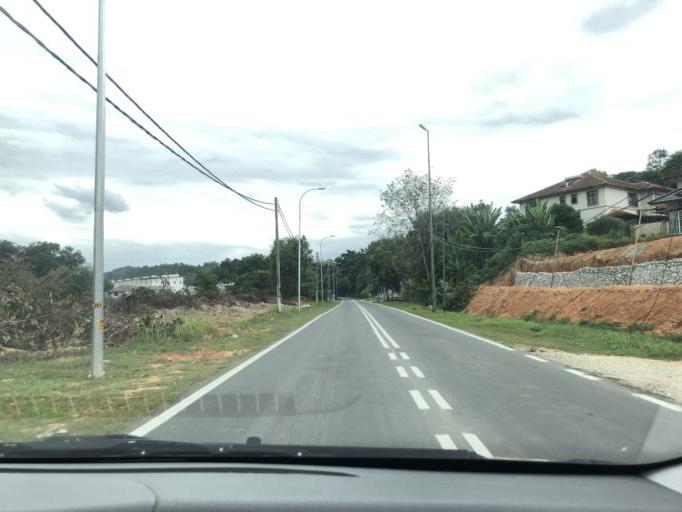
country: MY
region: Putrajaya
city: Putrajaya
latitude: 2.9185
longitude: 101.7504
